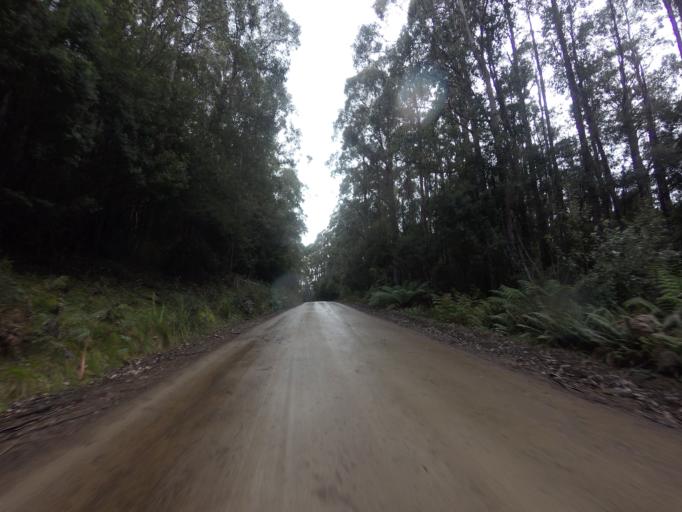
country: AU
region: Tasmania
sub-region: Huon Valley
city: Geeveston
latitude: -43.4840
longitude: 146.8917
